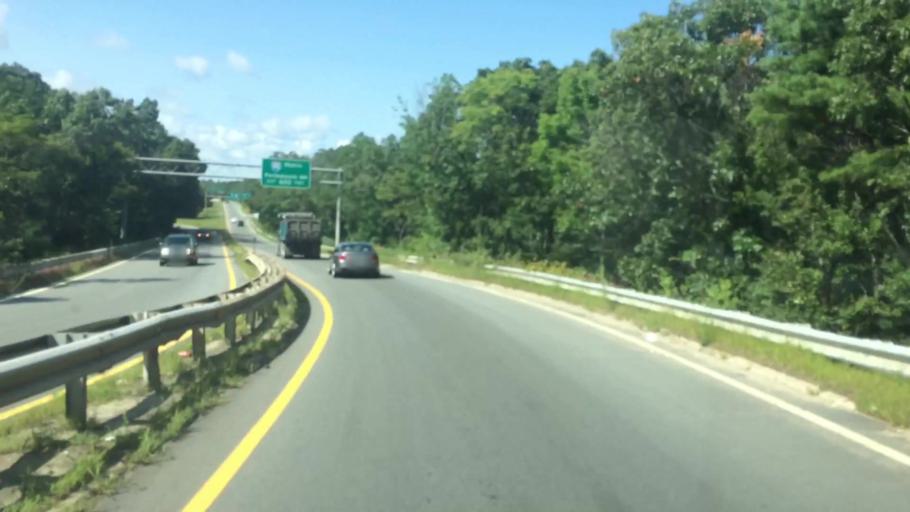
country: US
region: Massachusetts
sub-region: Essex County
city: South Peabody
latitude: 42.5141
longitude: -70.9910
